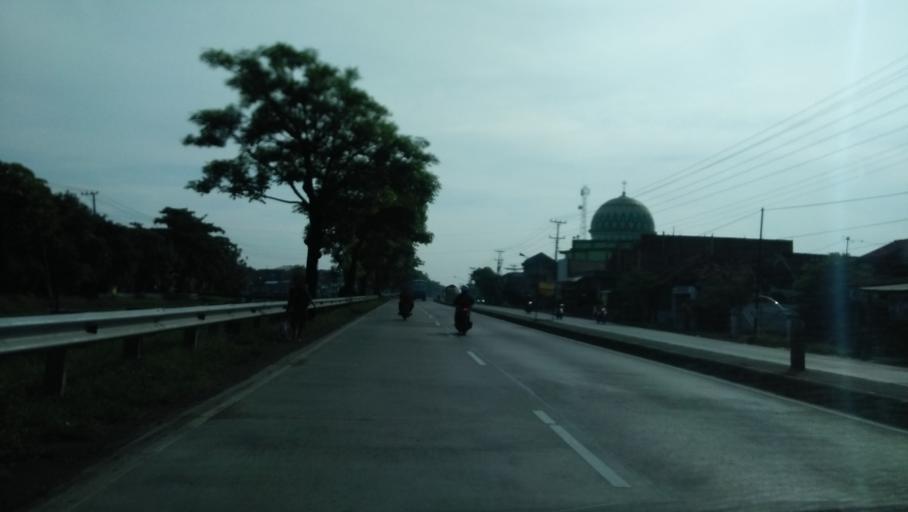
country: ID
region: Central Java
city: Demak
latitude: -6.9279
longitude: 110.5514
